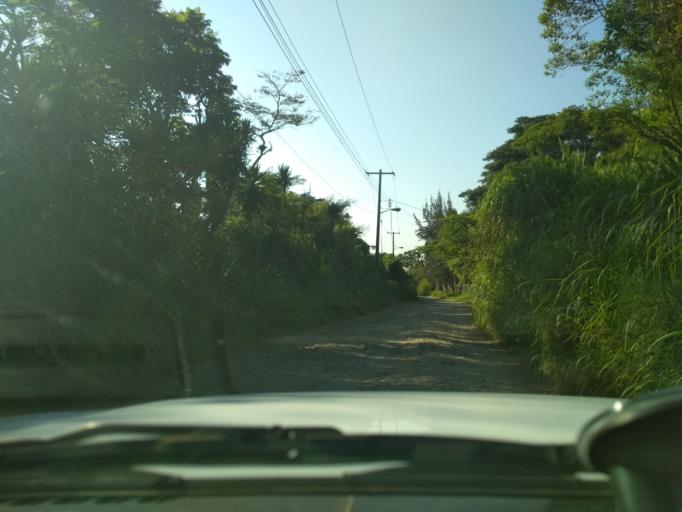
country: MX
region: Veracruz
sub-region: Fortin
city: Fraccionamiento Villas de la Llave
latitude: 18.9216
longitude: -96.9907
